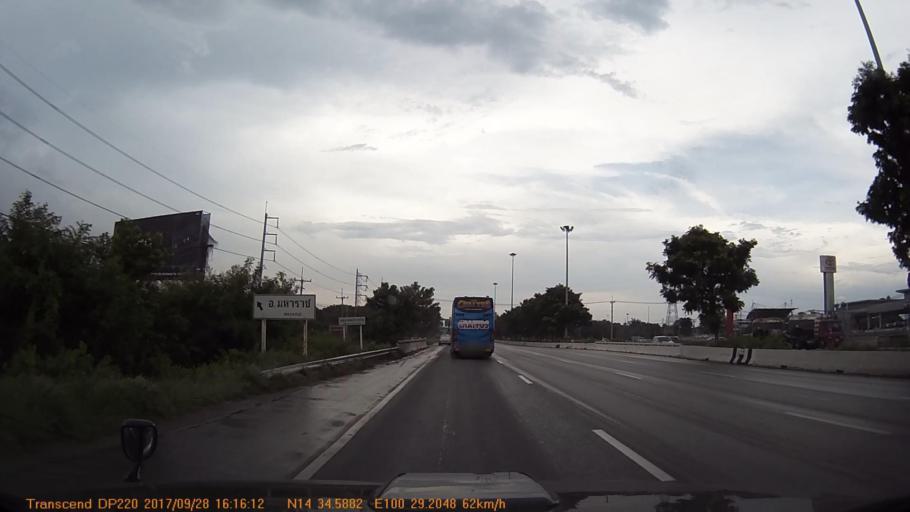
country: TH
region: Ang Thong
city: Ang Thong
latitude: 14.5769
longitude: 100.4864
